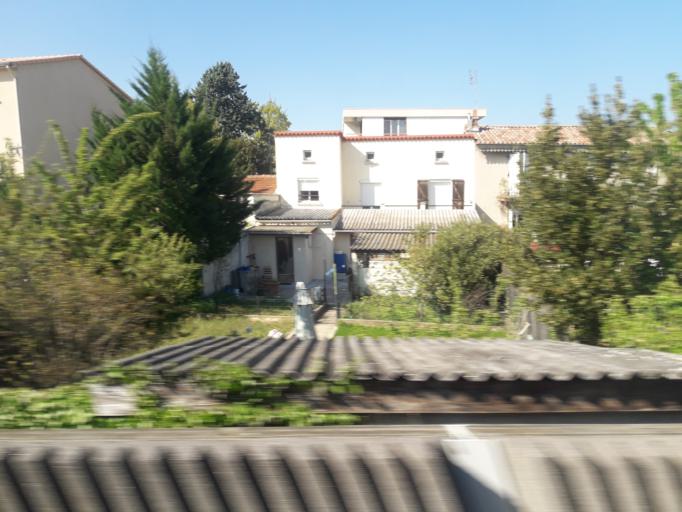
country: FR
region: Rhone-Alpes
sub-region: Departement de la Drome
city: Romans-sur-Isere
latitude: 45.0484
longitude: 5.0633
